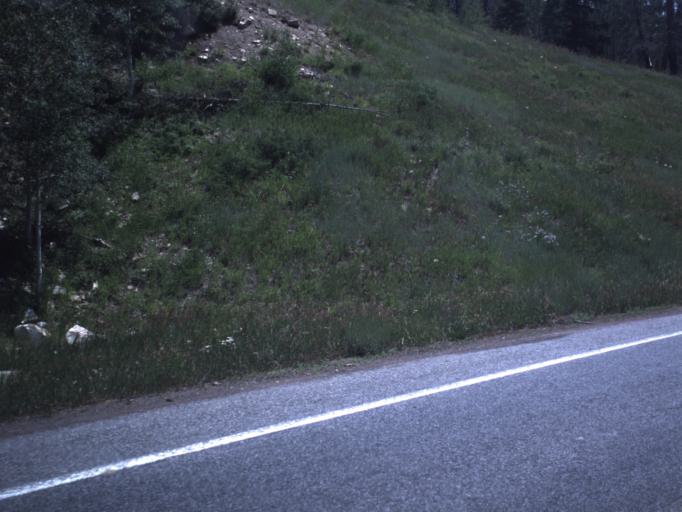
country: US
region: Utah
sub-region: Emery County
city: Huntington
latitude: 39.5364
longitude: -111.1564
